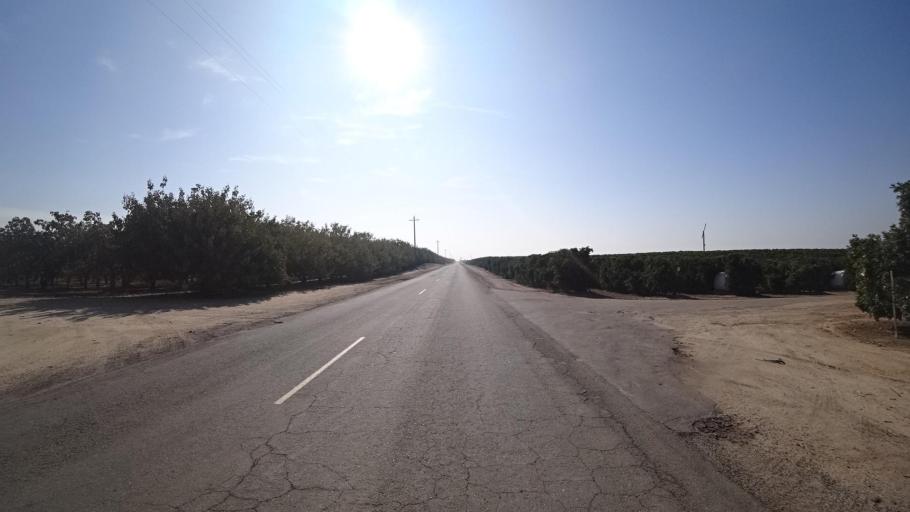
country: US
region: California
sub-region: Kern County
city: McFarland
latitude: 35.6096
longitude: -119.1688
